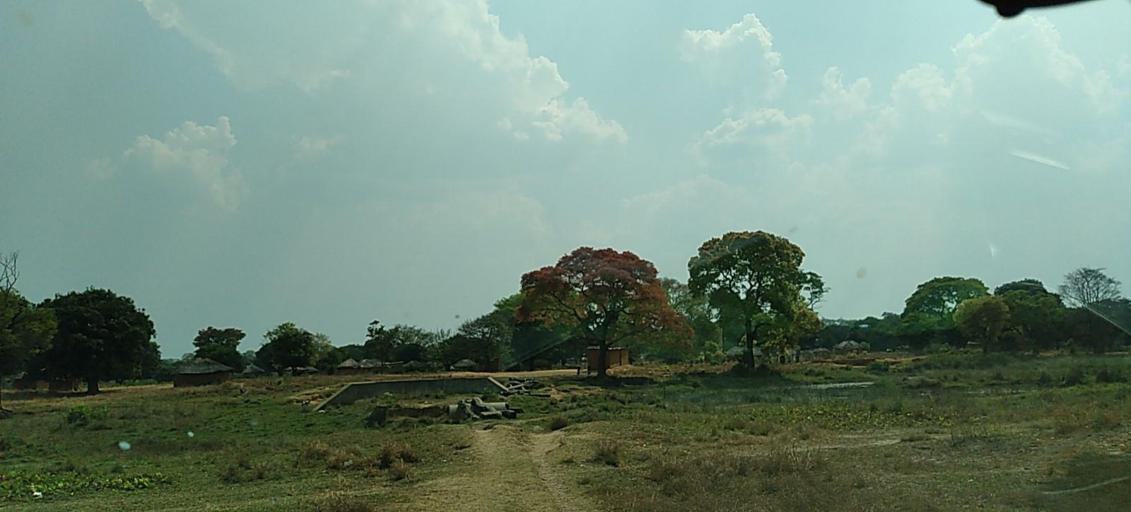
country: ZM
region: North-Western
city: Kabompo
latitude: -13.4478
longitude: 23.6635
